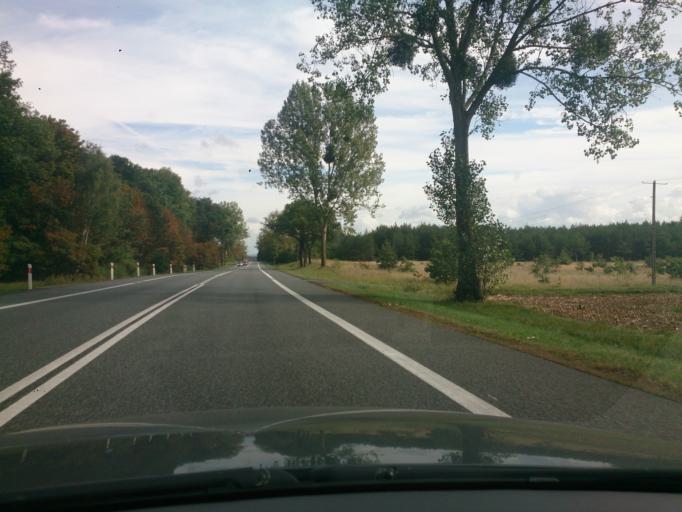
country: PL
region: Kujawsko-Pomorskie
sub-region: Powiat swiecki
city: Jezewo
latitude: 53.4510
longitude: 18.5750
